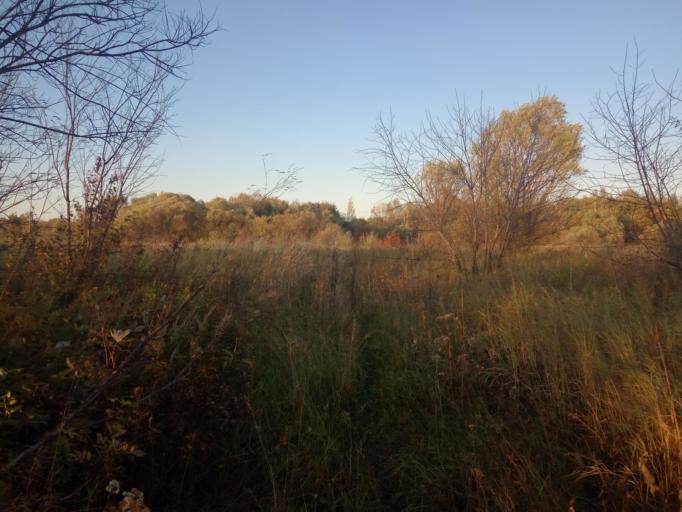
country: RU
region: Khabarovsk Krai
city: Khor
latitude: 47.7025
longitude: 134.9639
